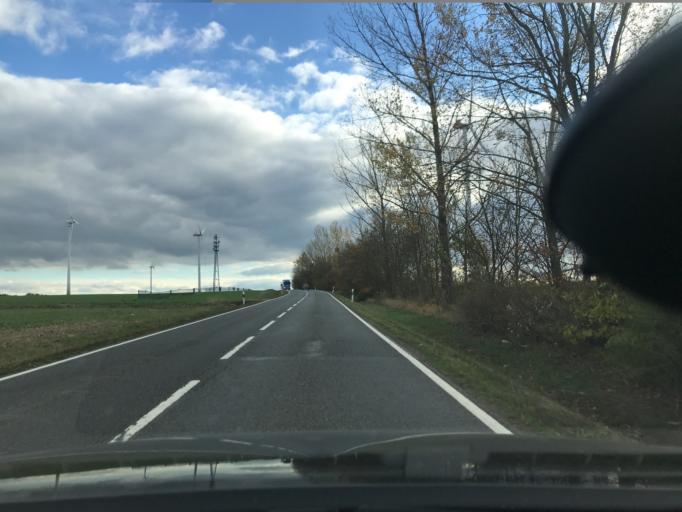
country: DE
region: Thuringia
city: Lauterbach
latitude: 51.0435
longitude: 10.3261
